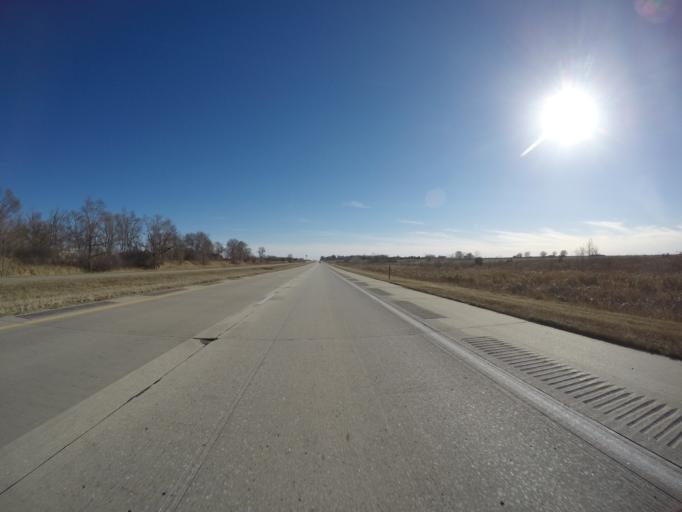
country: US
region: Nebraska
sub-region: Lancaster County
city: Hickman
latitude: 40.5196
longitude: -96.7071
